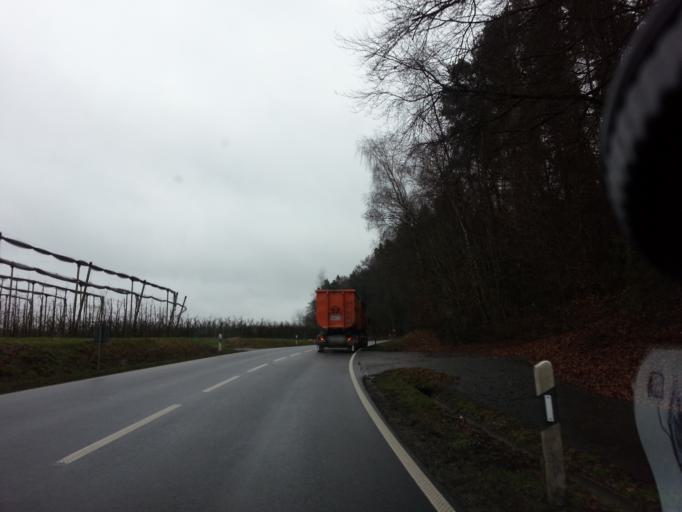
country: DE
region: Baden-Wuerttemberg
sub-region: Tuebingen Region
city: Oberteuringen
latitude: 47.6927
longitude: 9.4381
